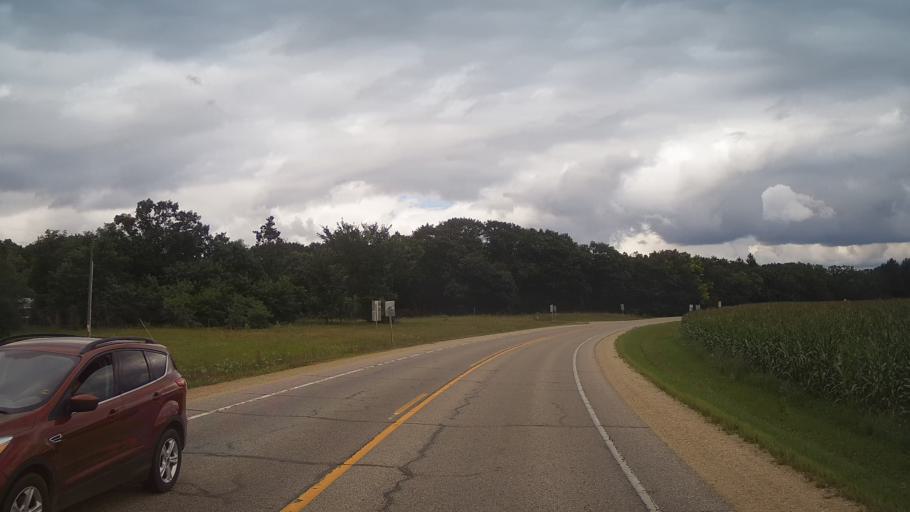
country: US
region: Wisconsin
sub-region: Waushara County
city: Wautoma
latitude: 44.0656
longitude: -89.3649
